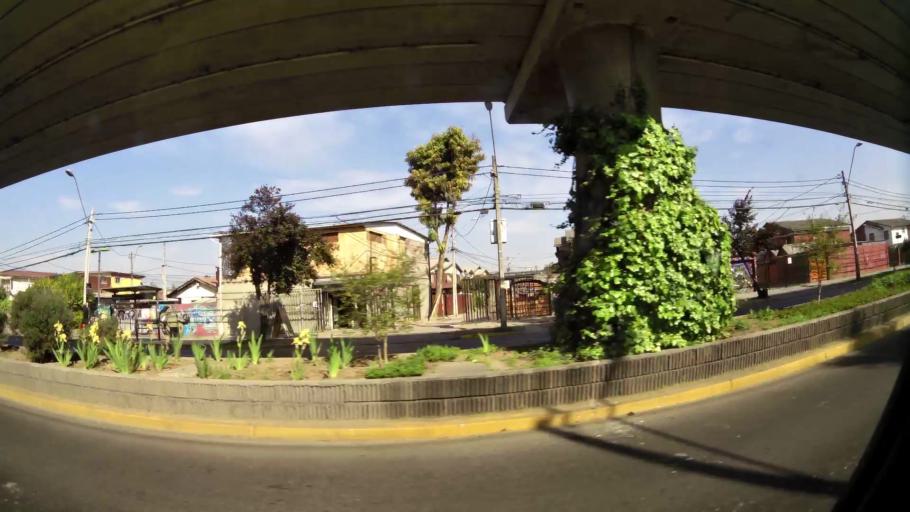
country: CL
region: Santiago Metropolitan
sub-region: Provincia de Santiago
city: Lo Prado
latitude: -33.4602
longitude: -70.7380
